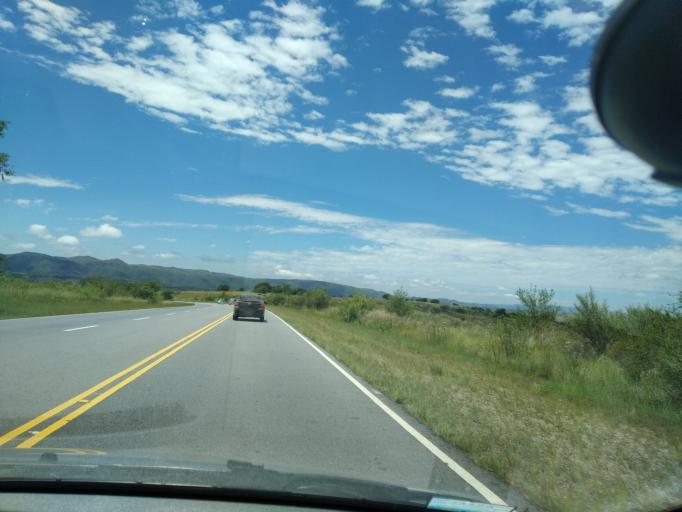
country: AR
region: Cordoba
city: Cuesta Blanca
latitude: -31.5861
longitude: -64.6206
